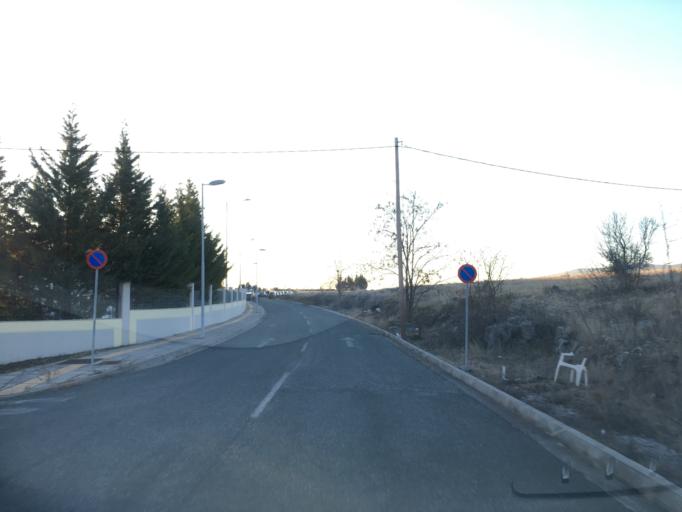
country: GR
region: West Macedonia
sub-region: Nomos Kozanis
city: Kozani
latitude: 40.2730
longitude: 21.7556
